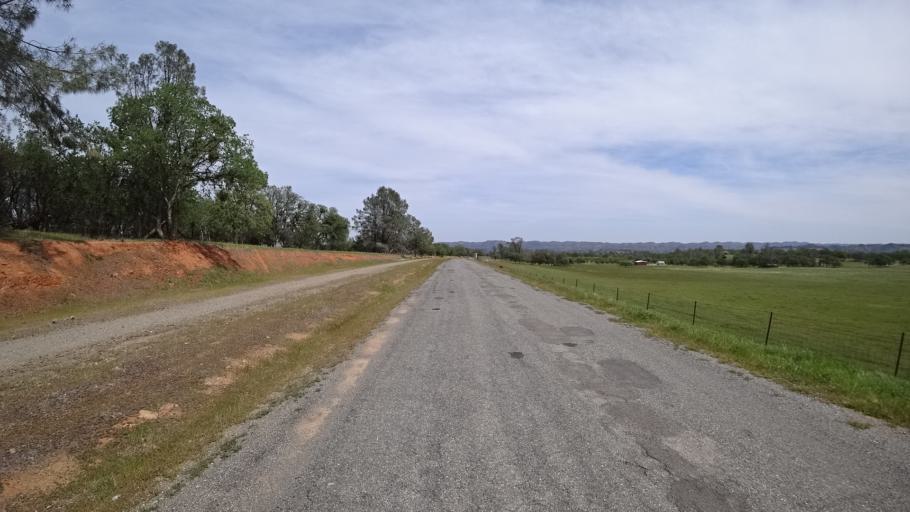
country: US
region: California
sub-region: Glenn County
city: Willows
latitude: 39.5757
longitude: -122.6103
